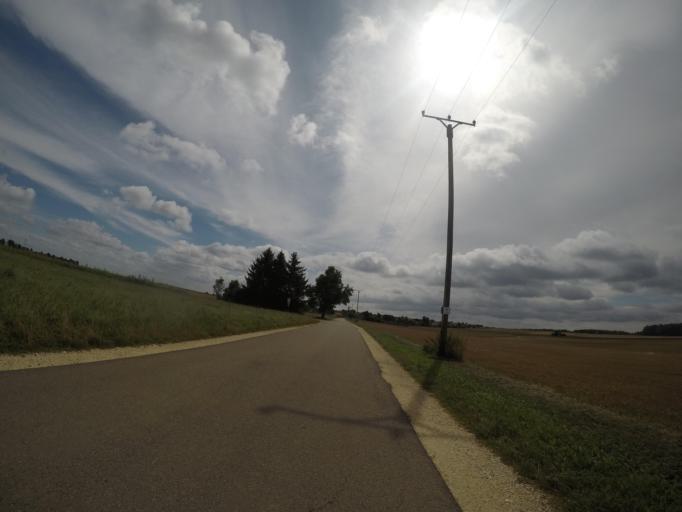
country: DE
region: Baden-Wuerttemberg
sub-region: Tuebingen Region
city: Schelklingen
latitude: 48.4214
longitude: 9.7331
